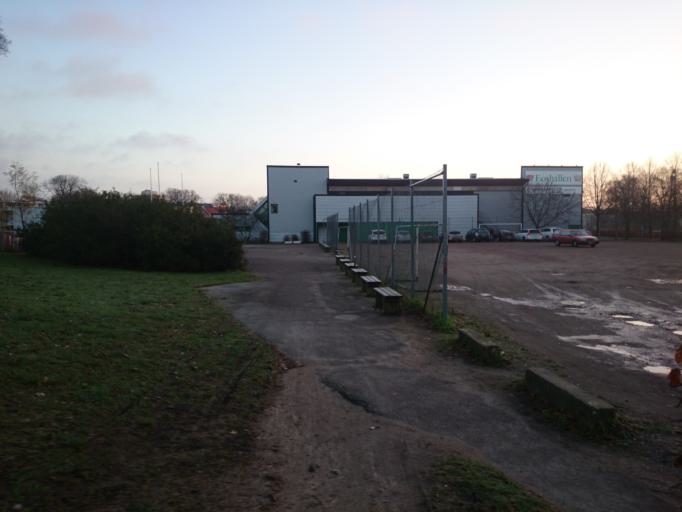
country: SE
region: Skane
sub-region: Lunds Kommun
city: Lund
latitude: 55.6963
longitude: 13.1997
